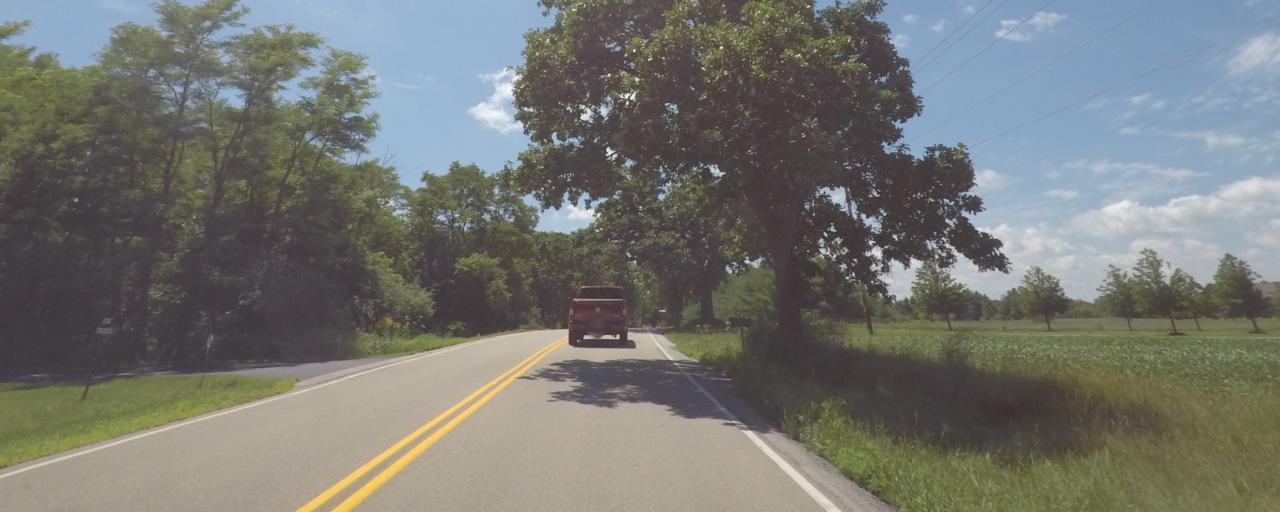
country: US
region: Wisconsin
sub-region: Waukesha County
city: Eagle
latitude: 42.9331
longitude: -88.5082
